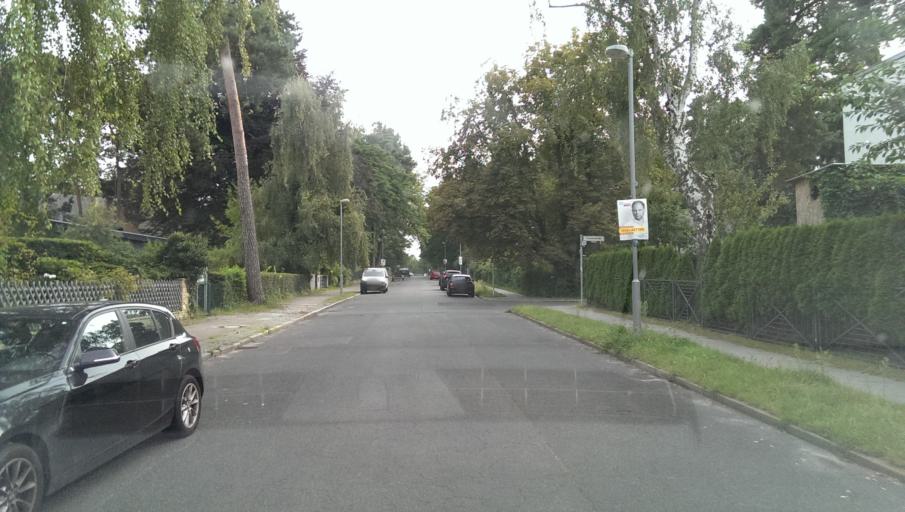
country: DE
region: Berlin
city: Zehlendorf Bezirk
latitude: 52.4433
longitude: 13.2284
